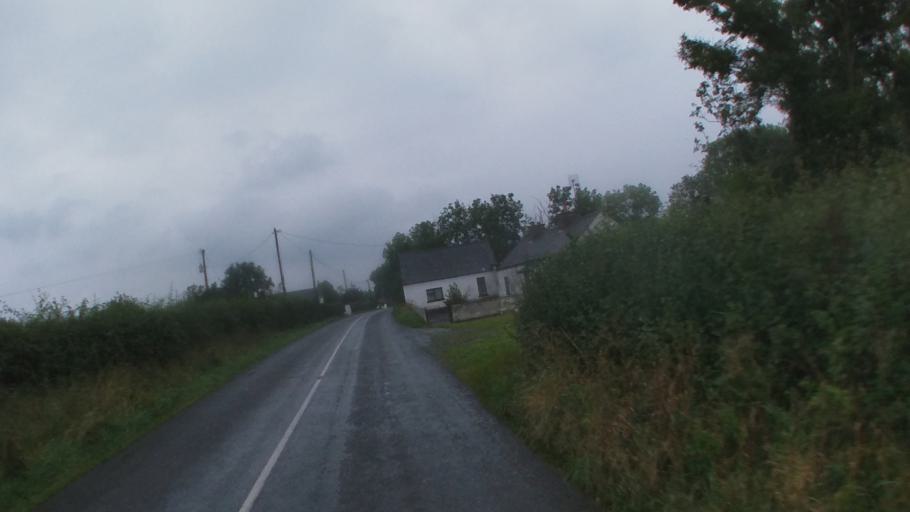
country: IE
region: Leinster
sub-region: Kilkenny
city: Callan
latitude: 52.5122
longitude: -7.4651
